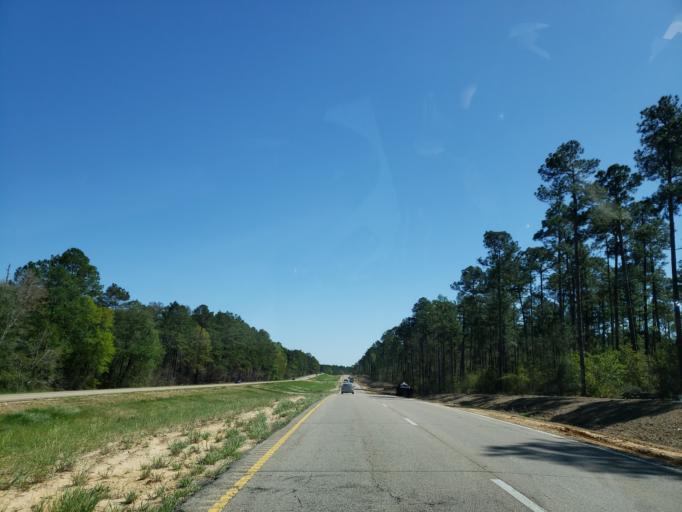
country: US
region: Mississippi
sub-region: Lamar County
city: Purvis
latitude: 31.1140
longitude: -89.2210
